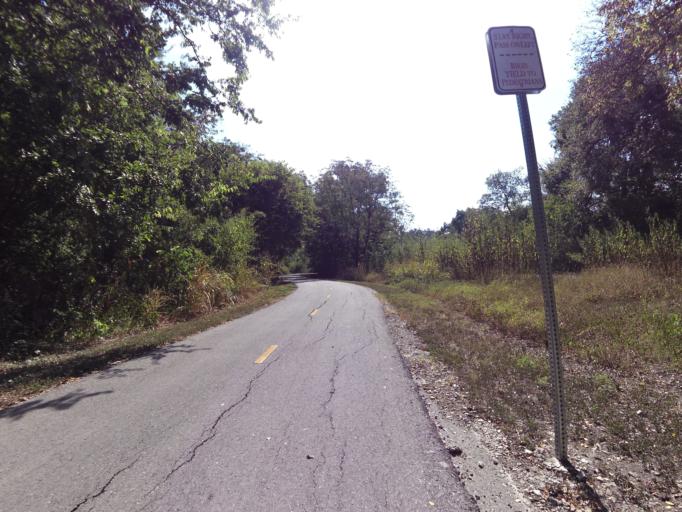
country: US
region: Texas
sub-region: Bexar County
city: Terrell Hills
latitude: 29.4491
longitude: -98.4225
